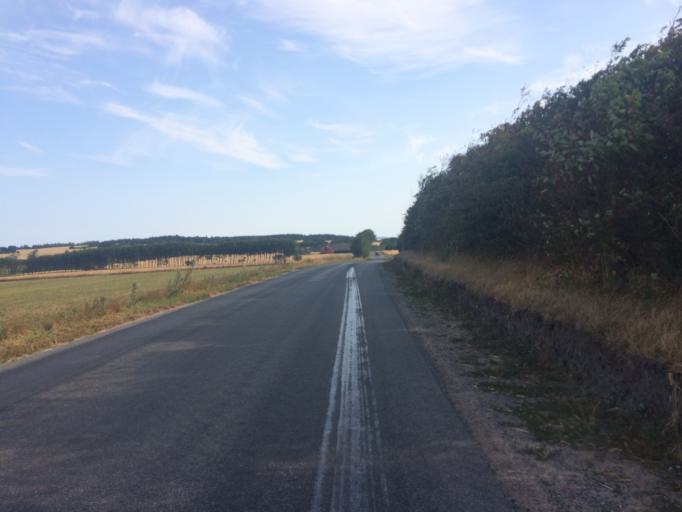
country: DK
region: Central Jutland
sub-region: Holstebro Kommune
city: Vinderup
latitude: 56.5936
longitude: 8.7568
